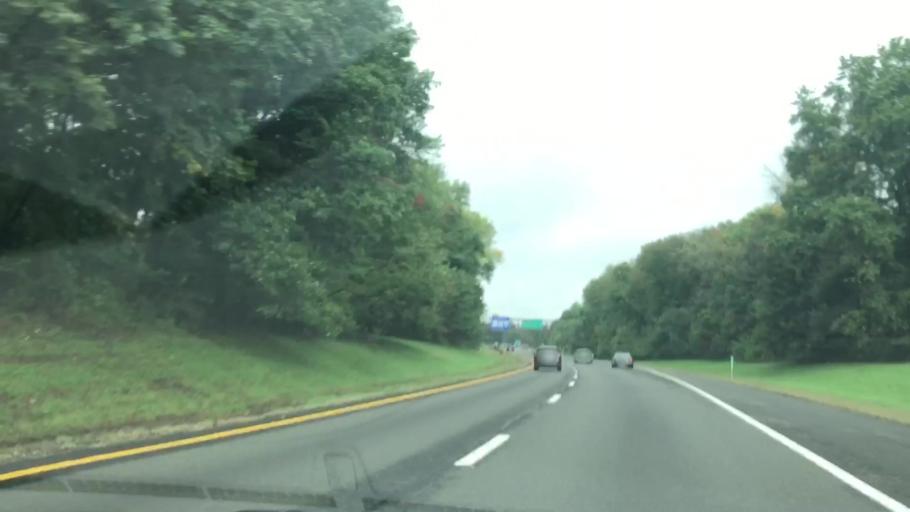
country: US
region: New Jersey
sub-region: Bergen County
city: Woodcliff Lake
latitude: 41.0315
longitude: -74.0691
